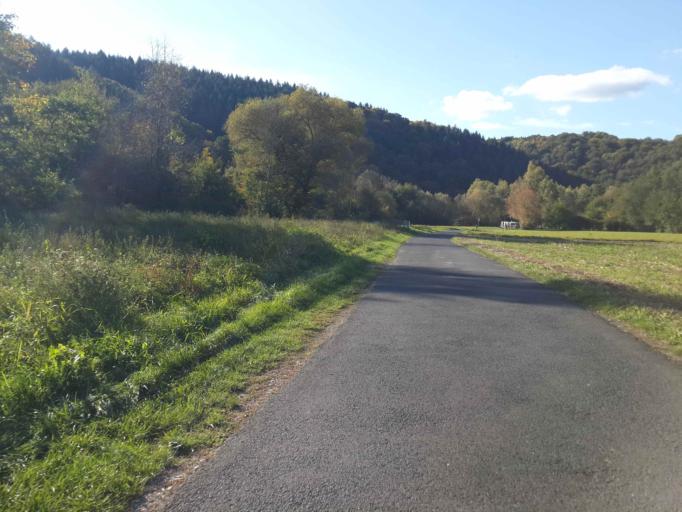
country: DE
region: Baden-Wuerttemberg
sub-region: Regierungsbezirk Stuttgart
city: Wertheim
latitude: 49.7305
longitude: 9.5234
